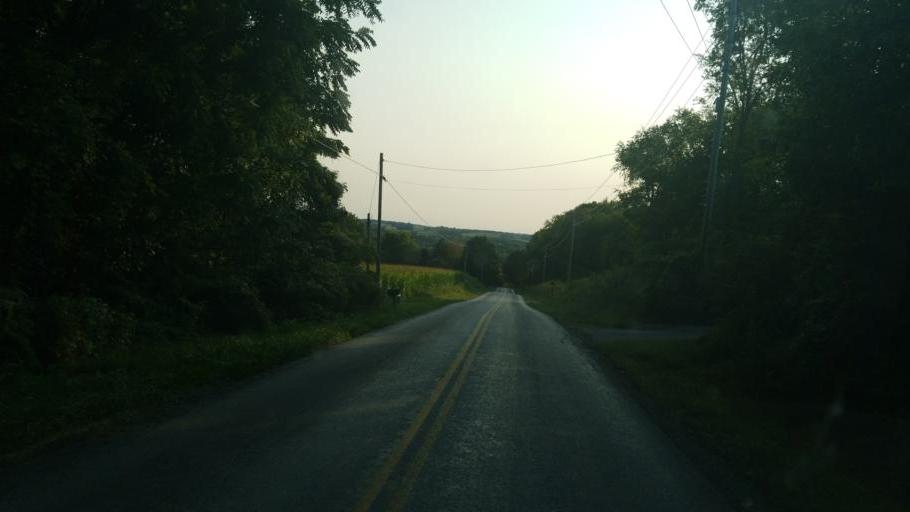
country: US
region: Ohio
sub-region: Wayne County
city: Shreve
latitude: 40.6700
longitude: -81.9406
